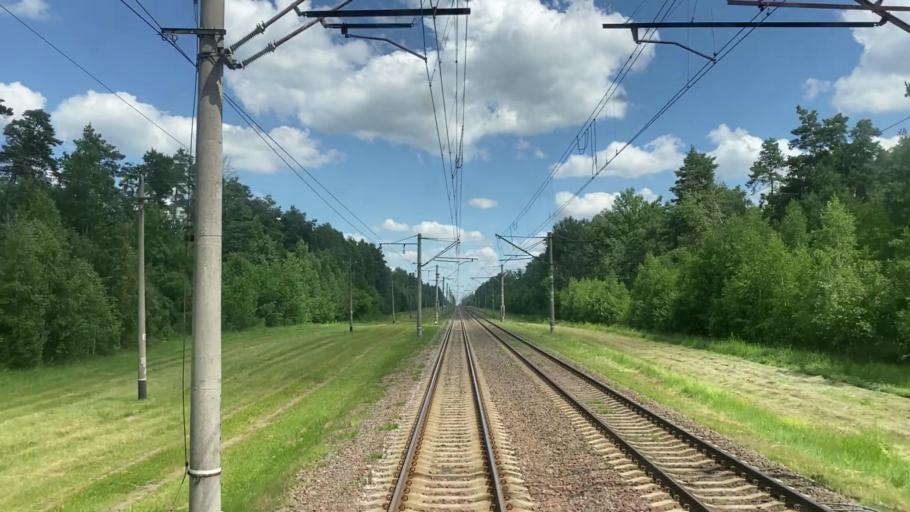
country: BY
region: Brest
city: Ivatsevichy
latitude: 52.7318
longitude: 25.3628
